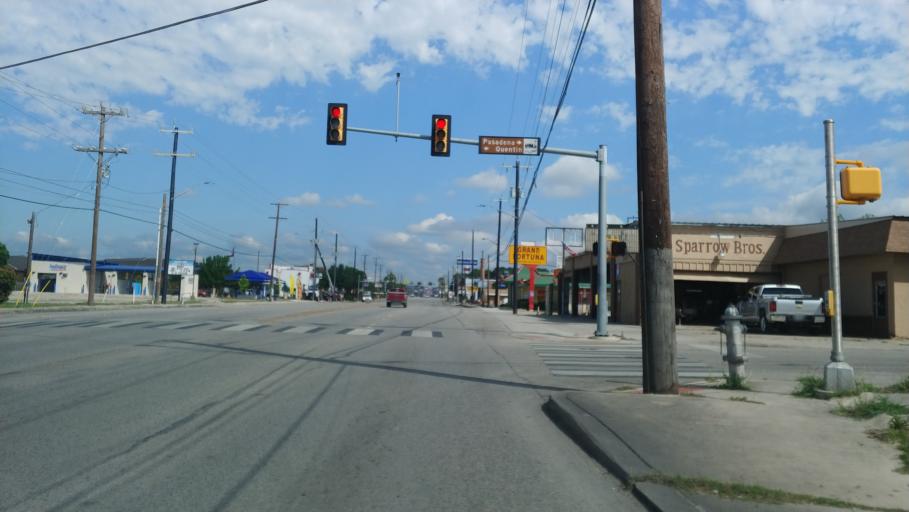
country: US
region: Texas
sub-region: Bexar County
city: Balcones Heights
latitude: 29.4682
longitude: -98.5297
